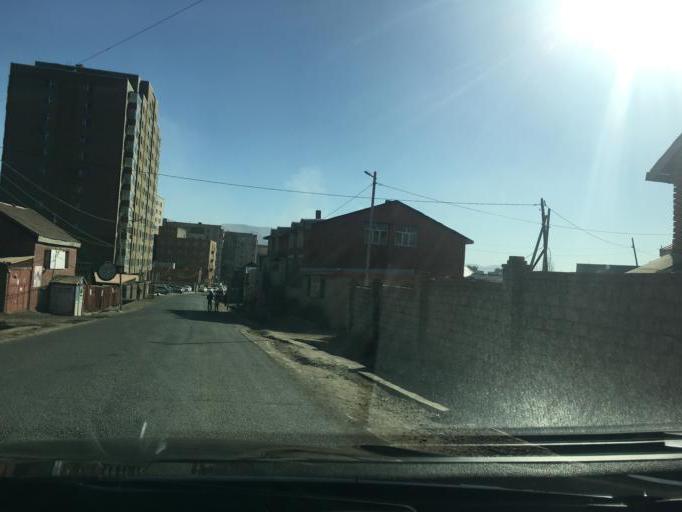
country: MN
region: Ulaanbaatar
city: Ulaanbaatar
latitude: 47.9297
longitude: 106.8769
